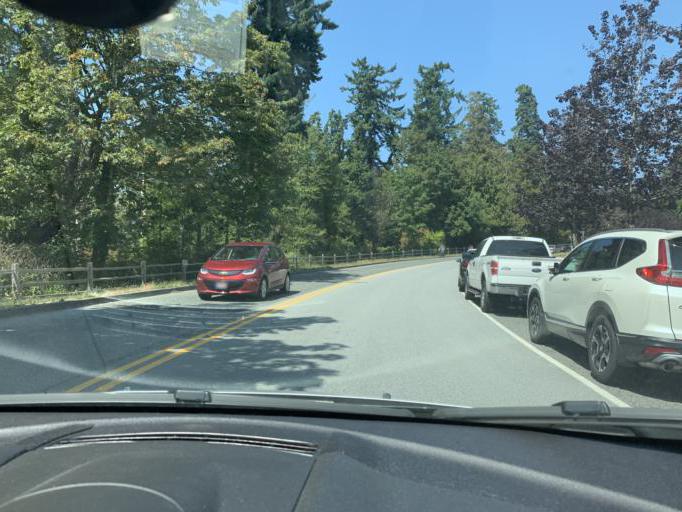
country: CA
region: British Columbia
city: West End
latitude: 49.2571
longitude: -123.2536
